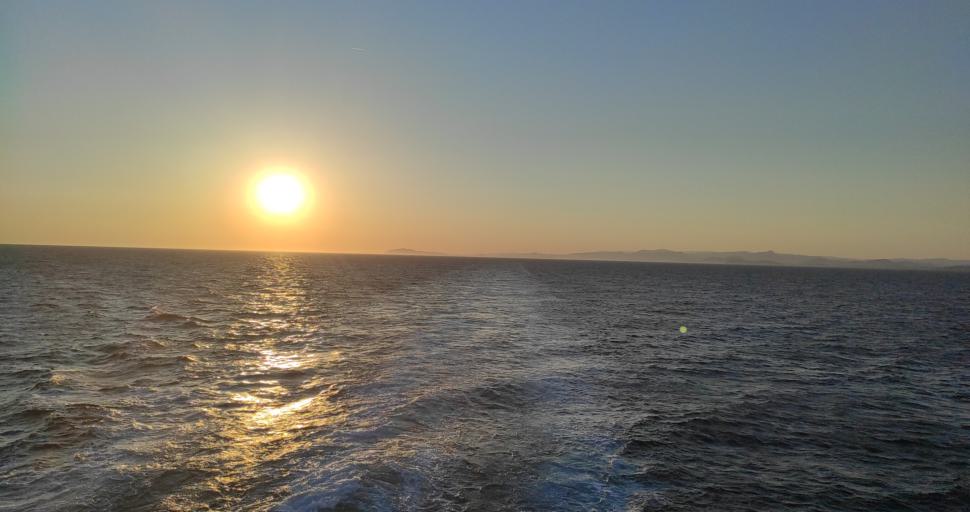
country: FR
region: Provence-Alpes-Cote d'Azur
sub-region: Departement du Var
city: Hyeres
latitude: 42.8793
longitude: 6.2277
